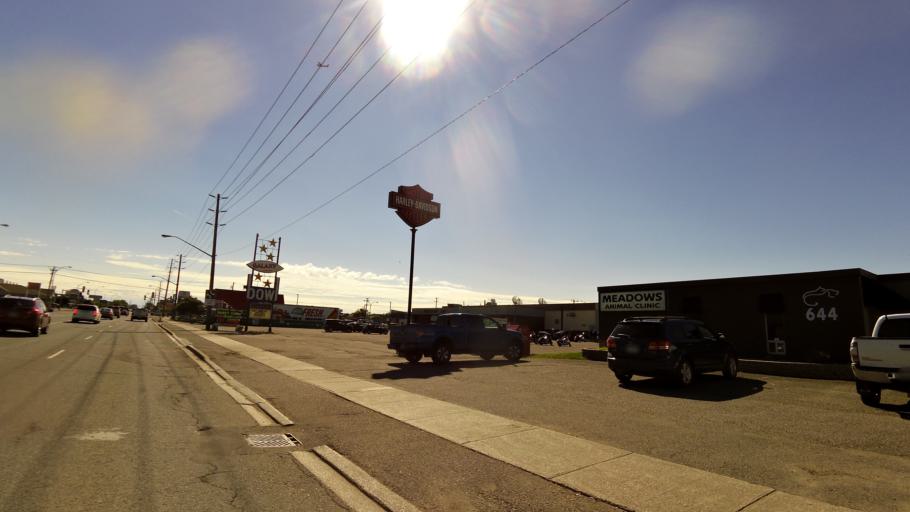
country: CA
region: Ontario
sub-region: Thunder Bay District
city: Thunder Bay
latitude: 48.3808
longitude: -89.2976
